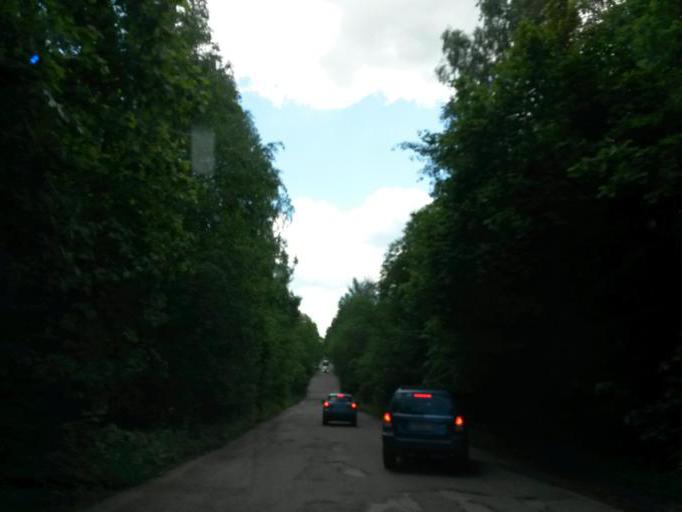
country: RU
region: Moskovskaya
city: Lyubuchany
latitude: 55.3059
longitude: 37.6151
